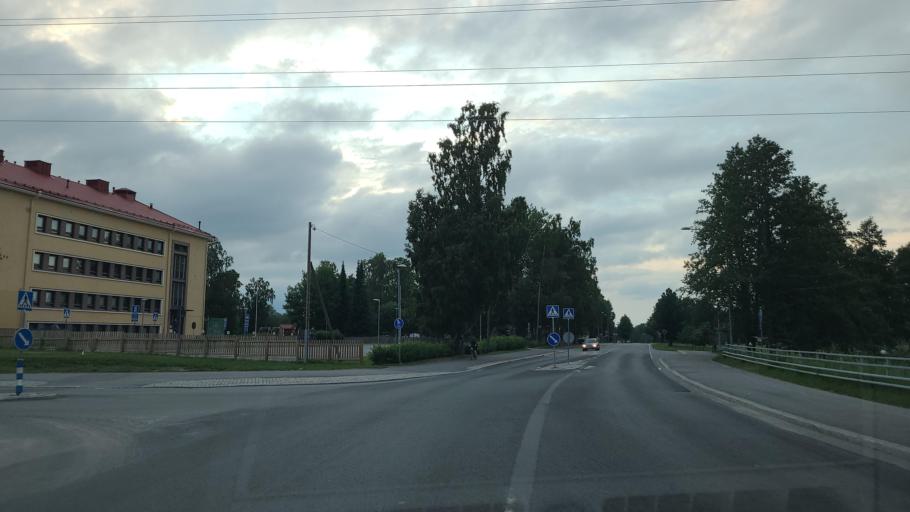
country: FI
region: Ostrobothnia
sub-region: Vaasa
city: Vaasa
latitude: 63.1049
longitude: 21.6176
